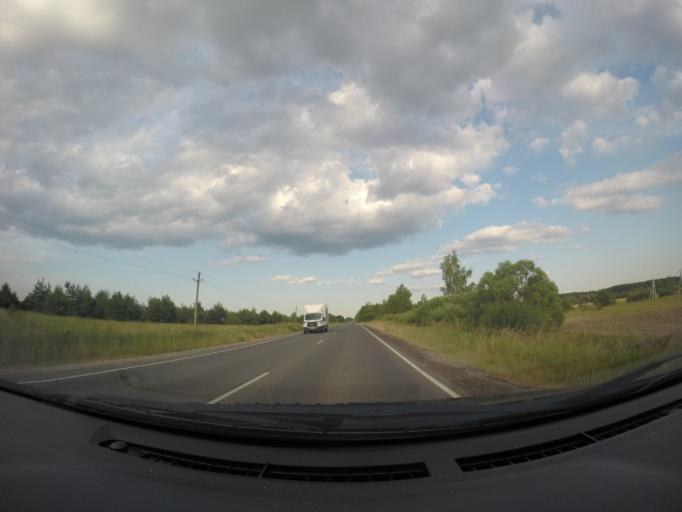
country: RU
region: Moskovskaya
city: Krasnyy Tkach
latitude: 55.4282
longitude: 39.2220
